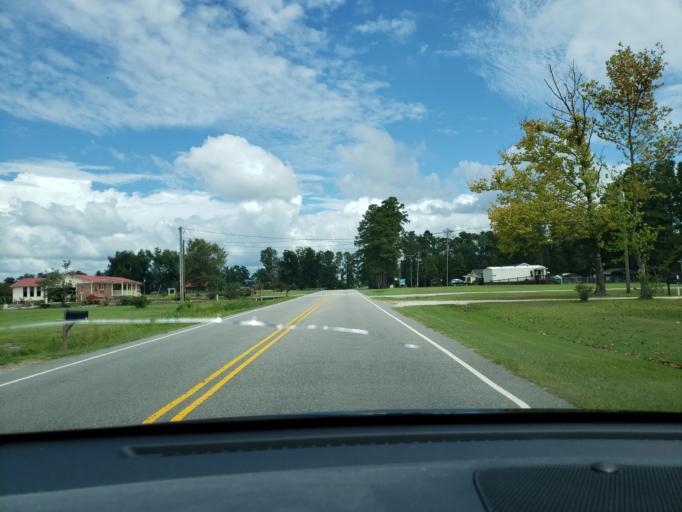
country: US
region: North Carolina
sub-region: Columbus County
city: Brunswick
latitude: 34.1985
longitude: -78.7663
